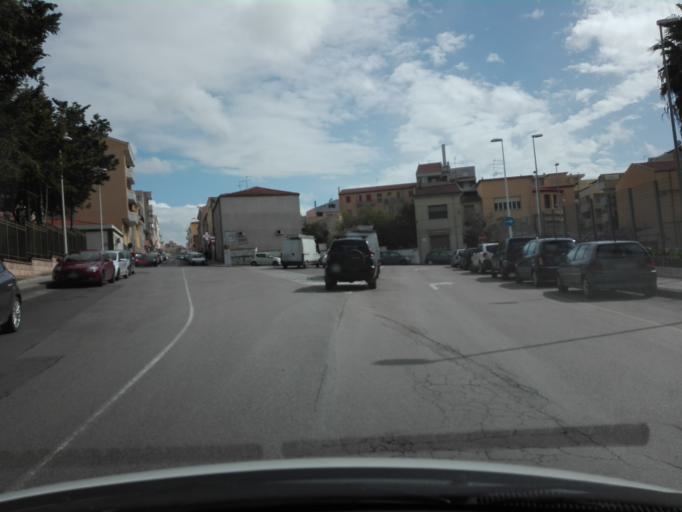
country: IT
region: Sardinia
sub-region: Provincia di Sassari
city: Sassari
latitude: 40.7358
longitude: 8.5643
